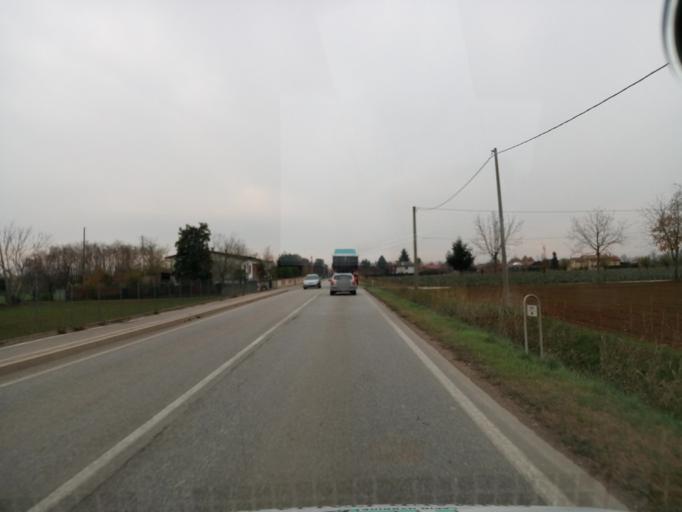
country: IT
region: Veneto
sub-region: Provincia di Treviso
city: Fanzolo
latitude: 45.7148
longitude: 12.0152
